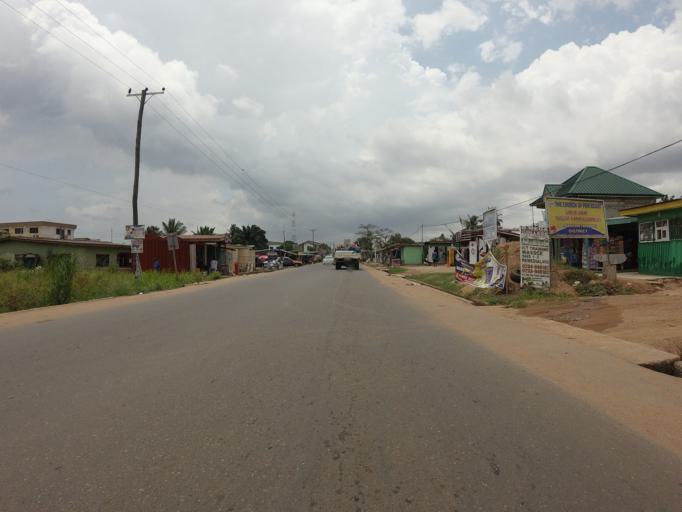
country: GH
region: Greater Accra
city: Medina Estates
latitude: 5.6863
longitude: -0.1654
